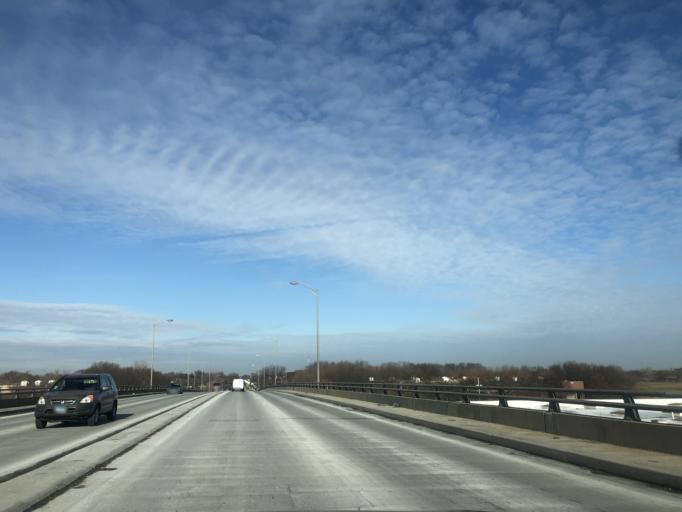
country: US
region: Illinois
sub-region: Cook County
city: Stickney
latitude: 41.8177
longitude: -87.7630
